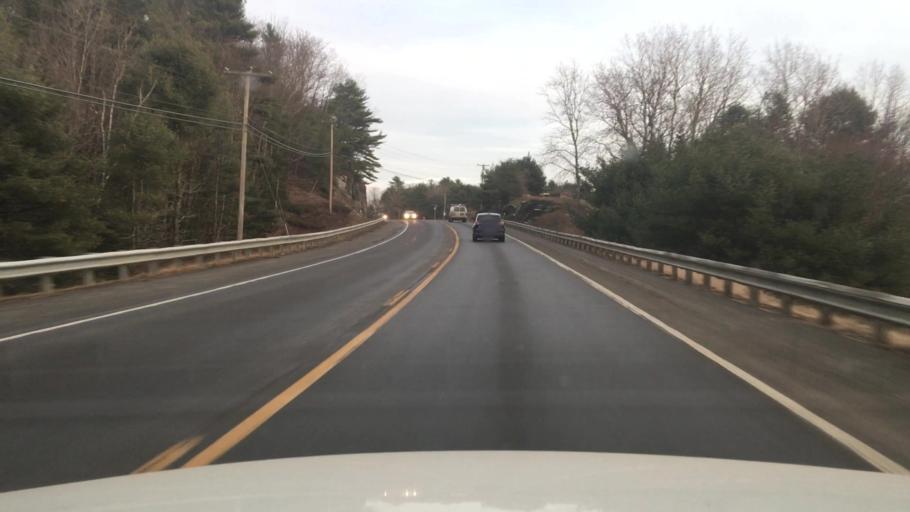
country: US
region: Maine
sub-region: Lincoln County
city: Edgecomb
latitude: 44.0017
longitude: -69.6202
